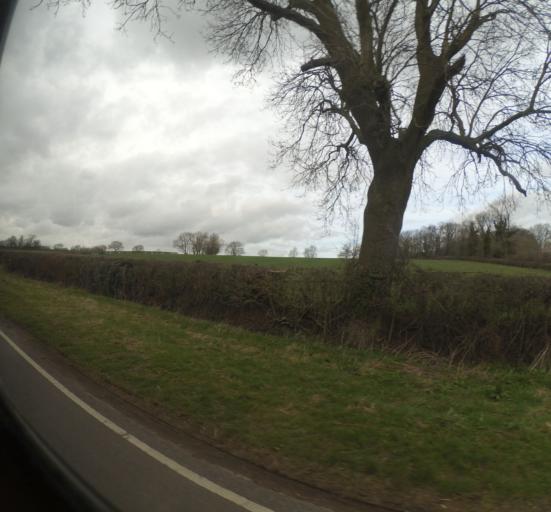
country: GB
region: England
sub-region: Warwickshire
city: Long Lawford
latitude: 52.4105
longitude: -1.3502
